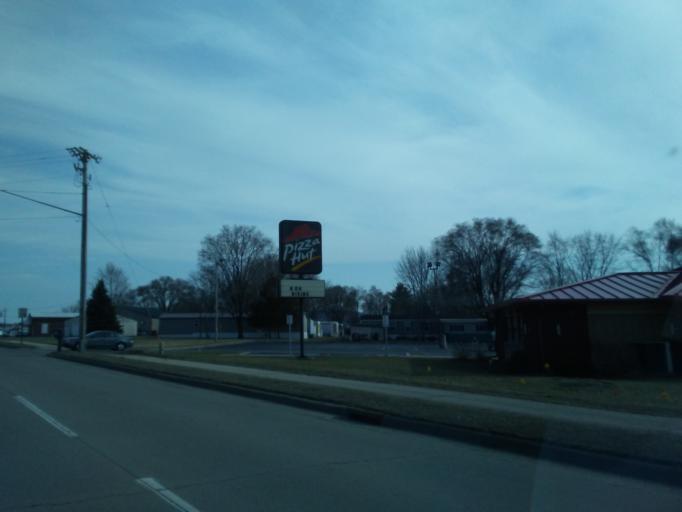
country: US
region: Wisconsin
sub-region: Crawford County
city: Prairie du Chien
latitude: 43.0342
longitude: -91.1368
